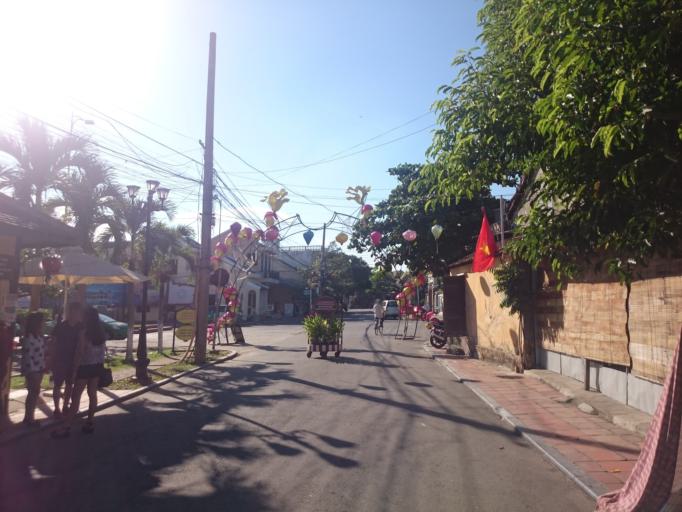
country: VN
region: Quang Nam
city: Hoi An
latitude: 15.8783
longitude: 108.3236
